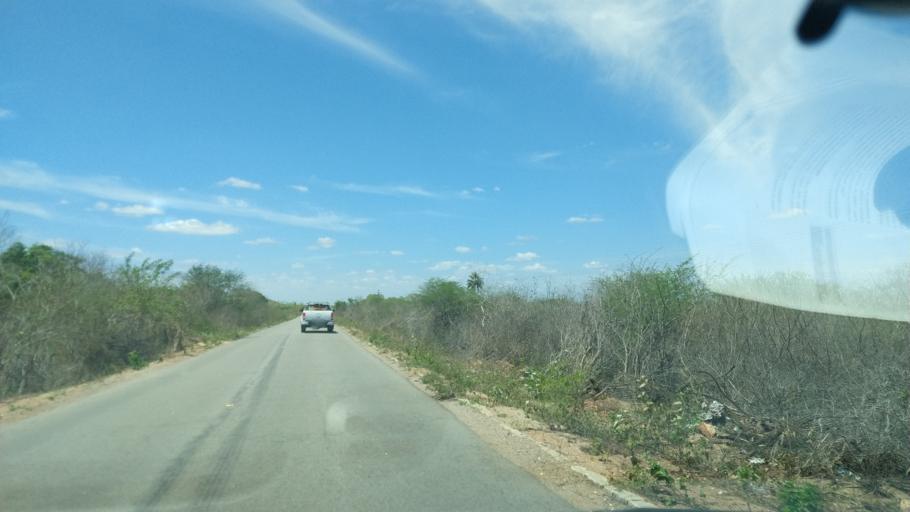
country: BR
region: Rio Grande do Norte
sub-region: Sao Paulo Do Potengi
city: Sao Paulo do Potengi
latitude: -5.9242
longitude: -35.5767
